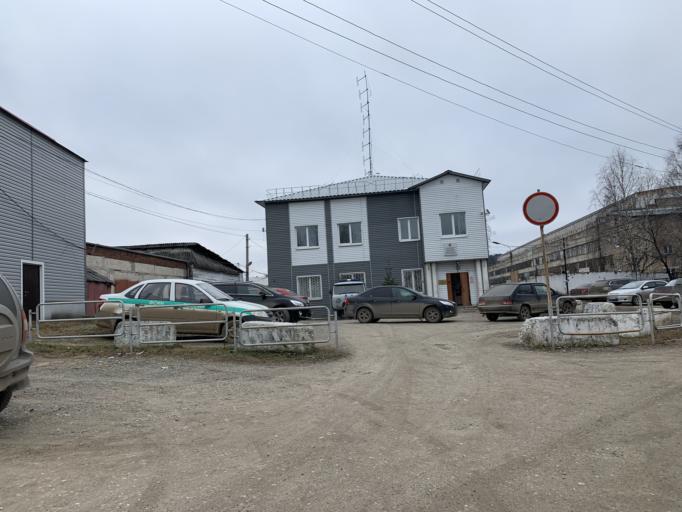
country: RU
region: Chelyabinsk
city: Nyazepetrovsk
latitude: 56.0527
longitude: 59.5916
